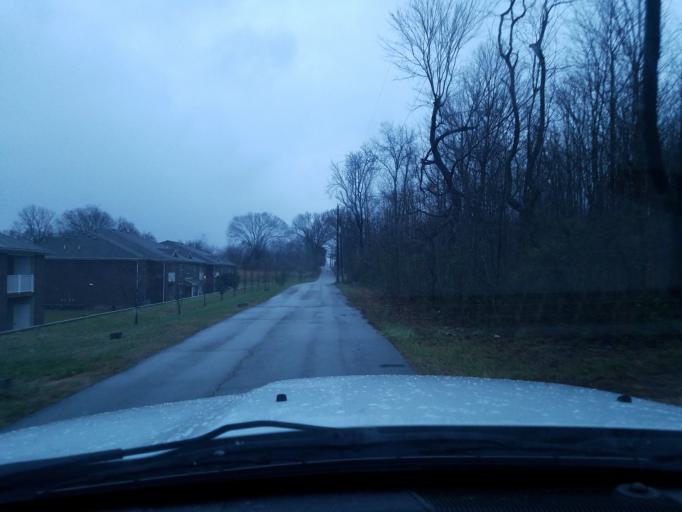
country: US
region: Indiana
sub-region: Clark County
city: Oak Park
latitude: 38.3360
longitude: -85.7032
